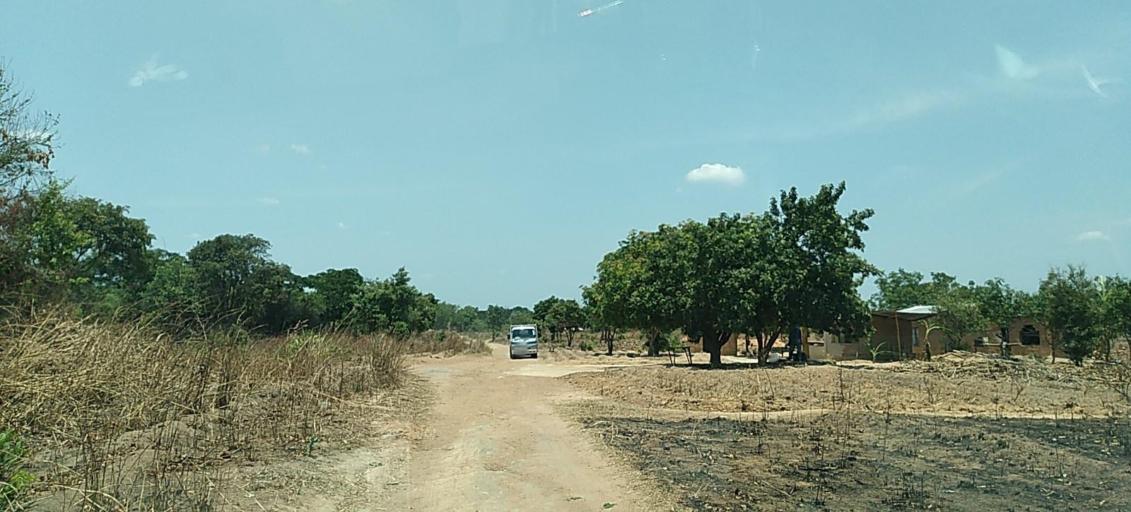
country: ZM
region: Copperbelt
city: Luanshya
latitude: -13.0709
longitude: 28.4067
